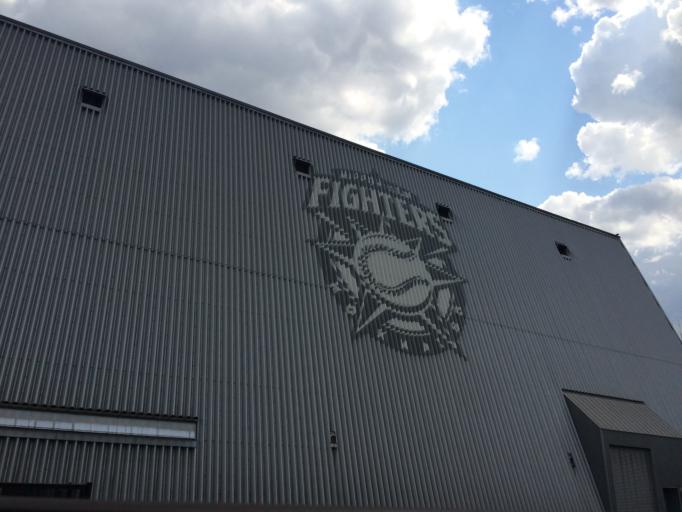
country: JP
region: Hokkaido
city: Sapporo
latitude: 43.0694
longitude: 141.3670
